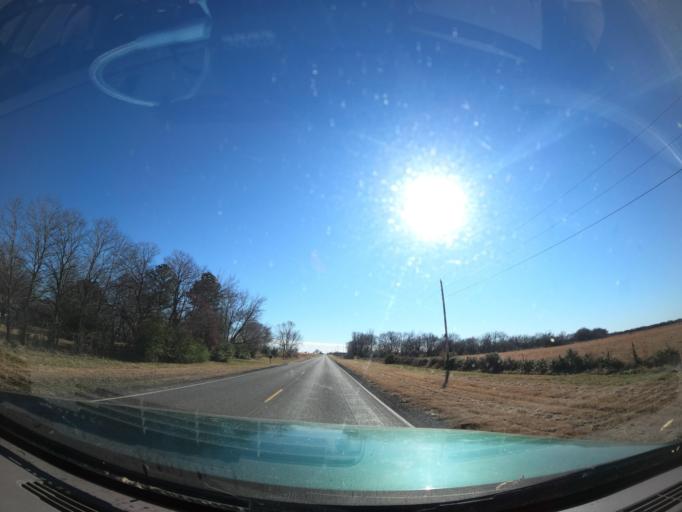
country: US
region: Oklahoma
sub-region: Muskogee County
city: Haskell
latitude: 35.6923
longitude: -95.6423
